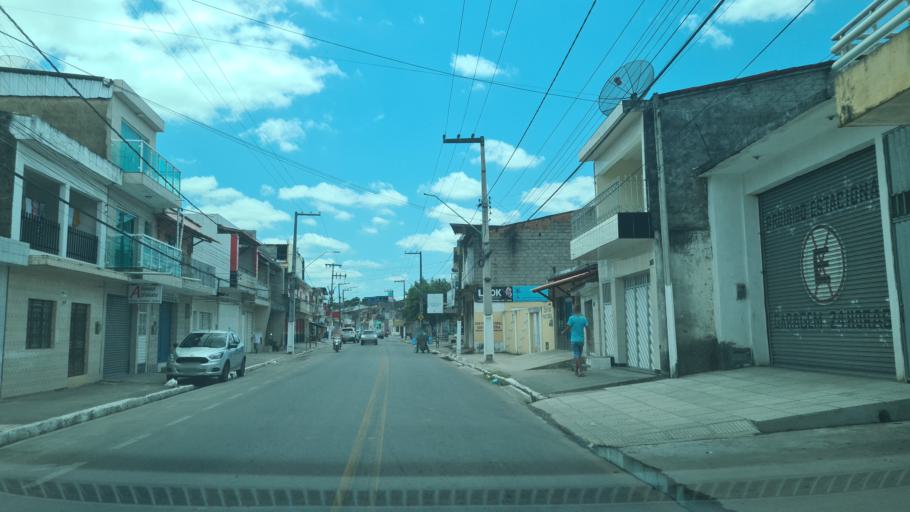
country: BR
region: Alagoas
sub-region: Uniao Dos Palmares
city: Uniao dos Palmares
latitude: -9.1614
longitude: -36.0290
